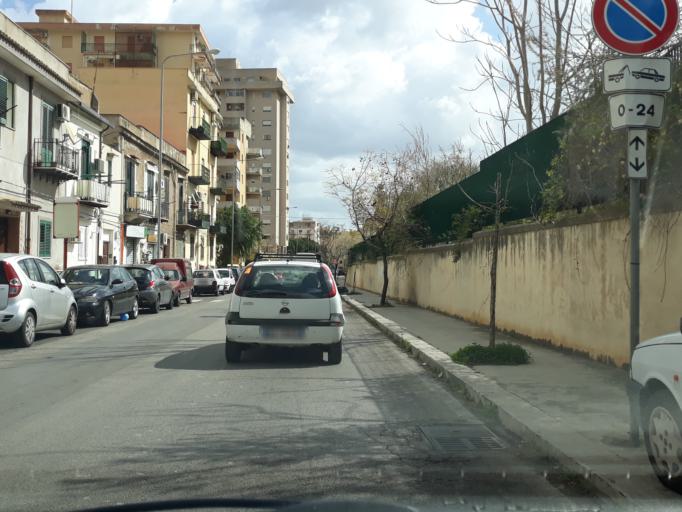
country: IT
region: Sicily
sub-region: Palermo
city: Palermo
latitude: 38.1228
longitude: 13.3261
